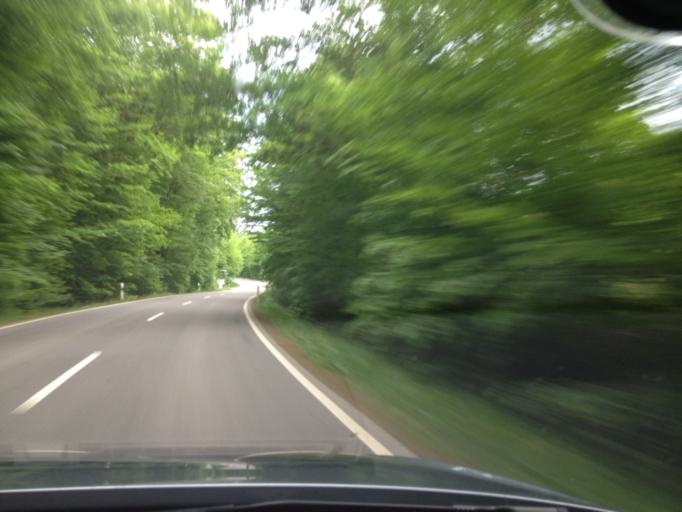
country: DE
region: Saarland
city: Spiesen-Elversberg
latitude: 49.3252
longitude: 7.1238
